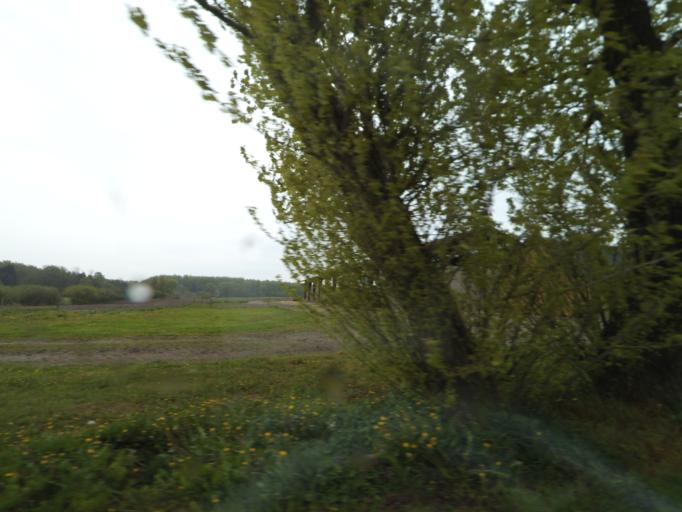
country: DK
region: South Denmark
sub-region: Faaborg-Midtfyn Kommune
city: Ringe
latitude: 55.1868
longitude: 10.5718
